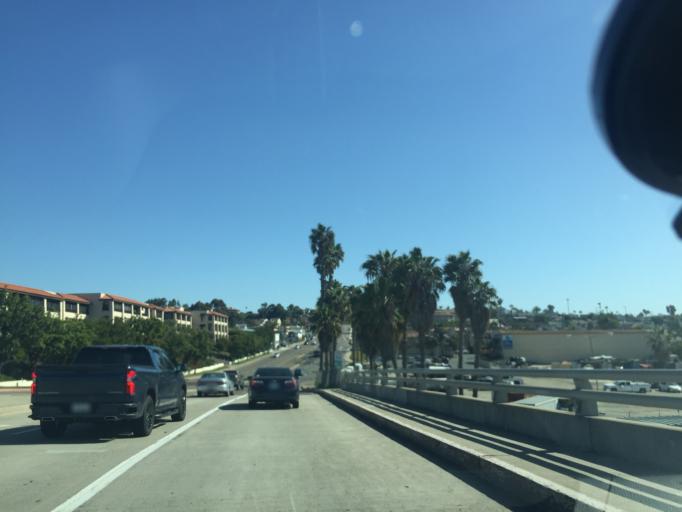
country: US
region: California
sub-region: San Diego County
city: La Jolla
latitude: 32.7906
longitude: -117.2061
